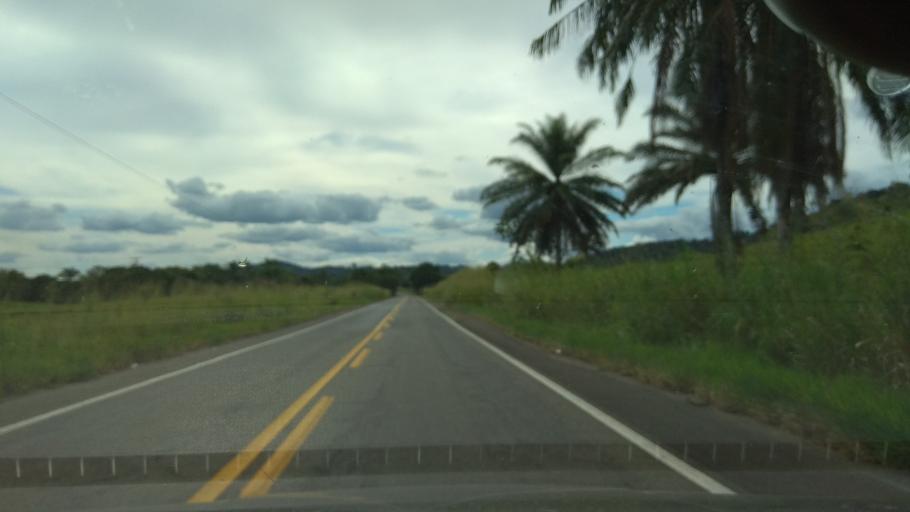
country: BR
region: Bahia
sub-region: Ipiau
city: Ipiau
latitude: -14.1864
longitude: -39.6602
